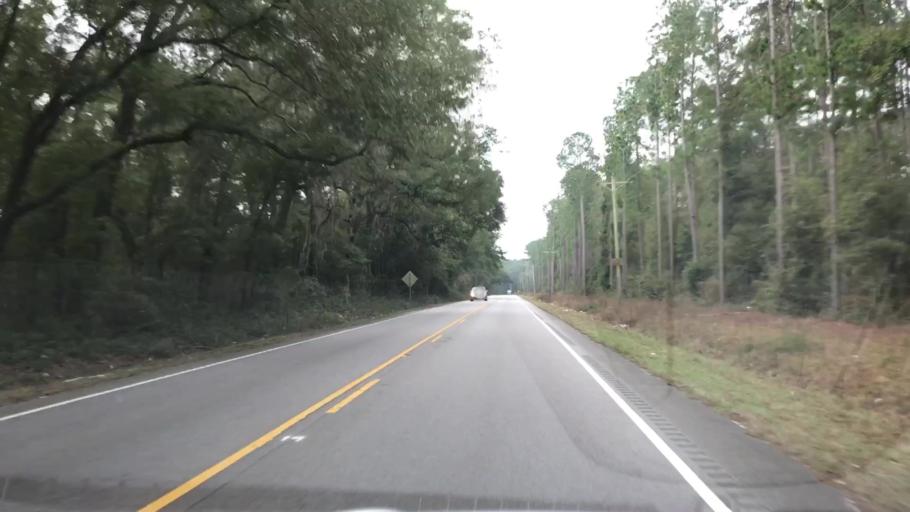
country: US
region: South Carolina
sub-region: Jasper County
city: Ridgeland
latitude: 32.4945
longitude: -80.8856
